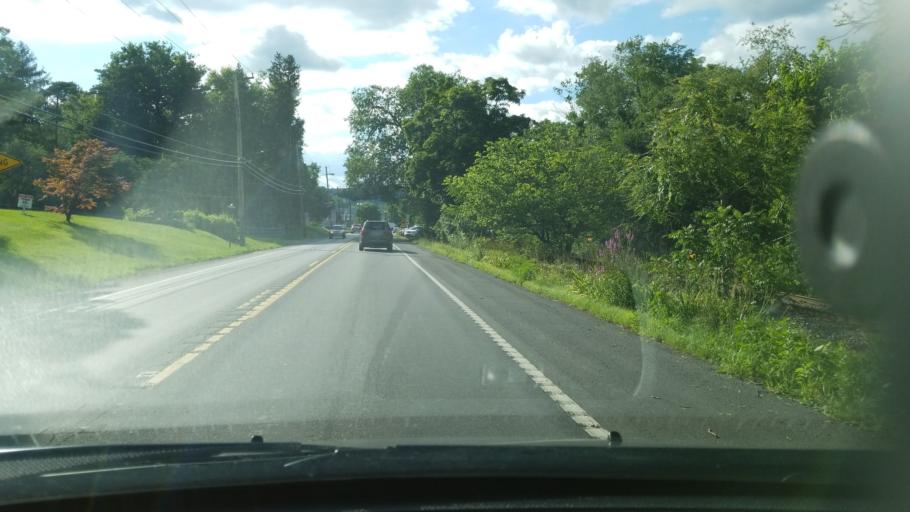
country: US
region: Pennsylvania
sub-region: Northumberland County
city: Riverside
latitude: 40.9540
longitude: -76.6209
